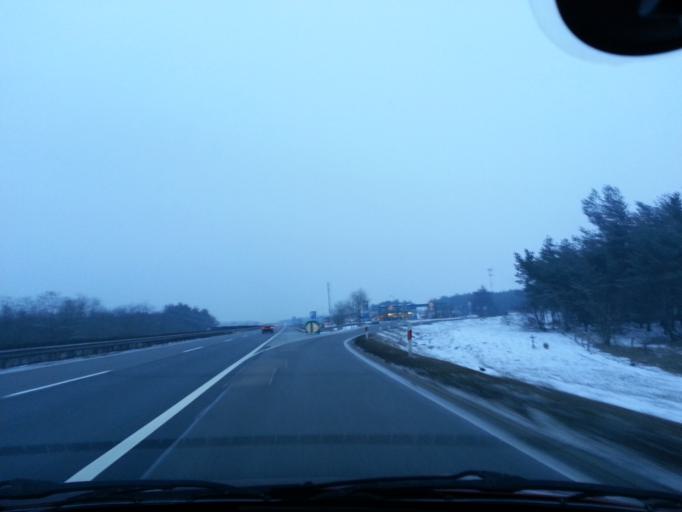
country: HU
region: Pest
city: Inarcs
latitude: 47.2778
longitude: 19.3214
